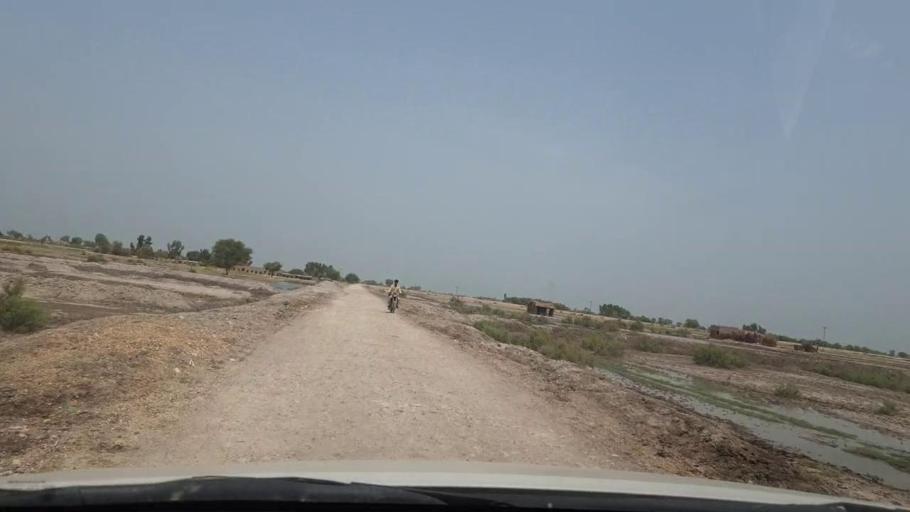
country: PK
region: Sindh
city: Rustam jo Goth
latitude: 28.0747
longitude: 68.8179
